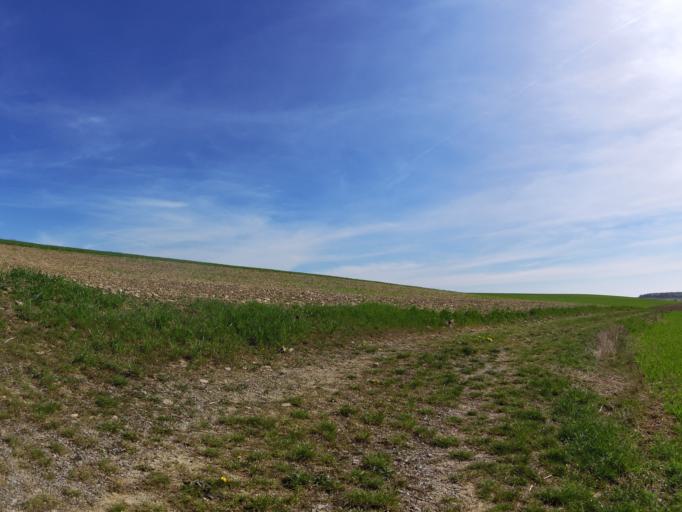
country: DE
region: Bavaria
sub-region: Regierungsbezirk Unterfranken
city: Rimpar
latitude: 49.8601
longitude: 9.9716
